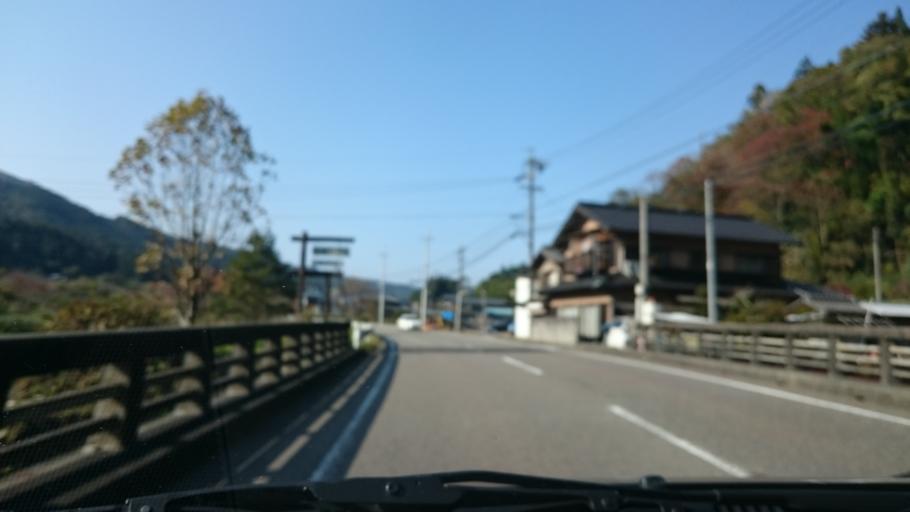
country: JP
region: Gifu
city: Nakatsugawa
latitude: 35.7241
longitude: 137.3552
